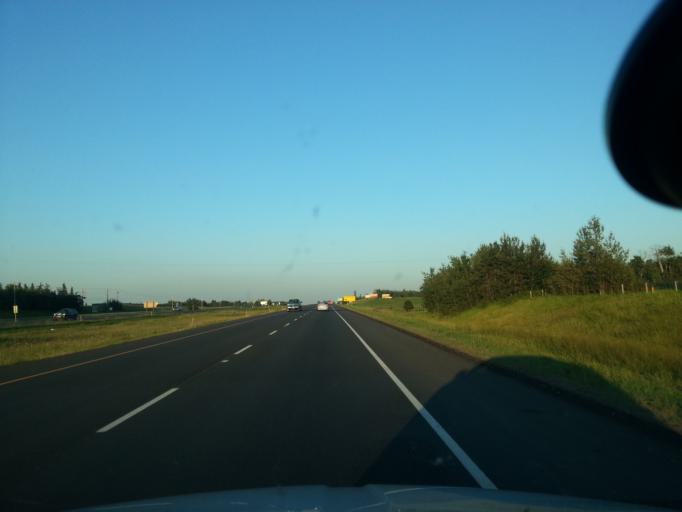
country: CA
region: Alberta
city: St. Albert
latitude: 53.5695
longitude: -113.7278
